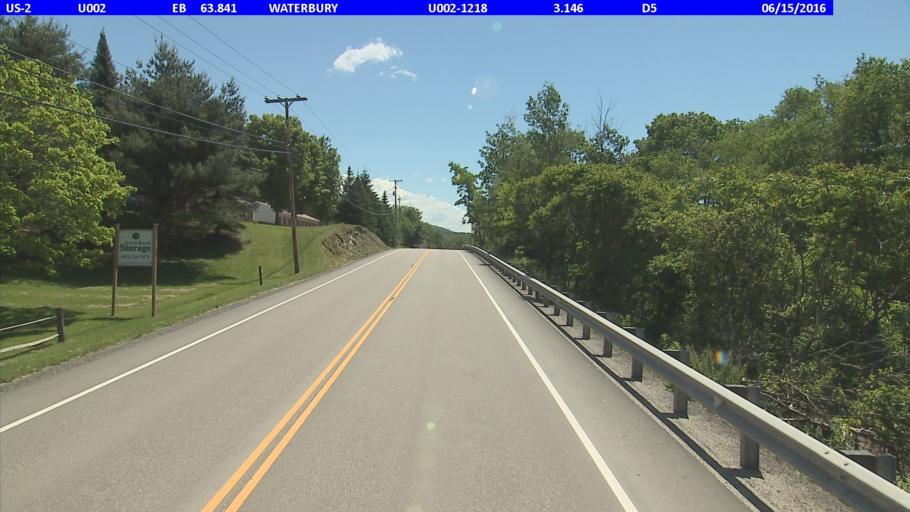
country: US
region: Vermont
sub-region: Washington County
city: Waterbury
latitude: 44.3465
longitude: -72.7693
